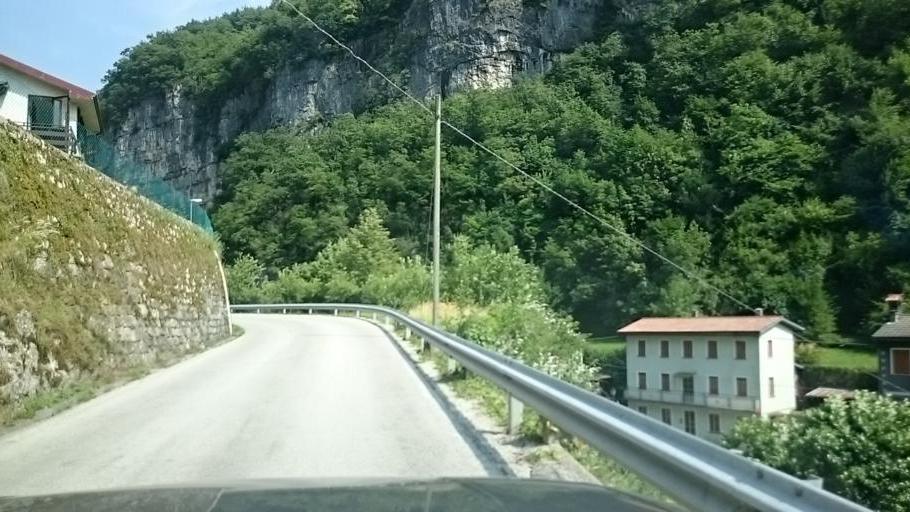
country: IT
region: Veneto
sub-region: Provincia di Vicenza
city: Valstagna
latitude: 45.8607
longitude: 11.6560
